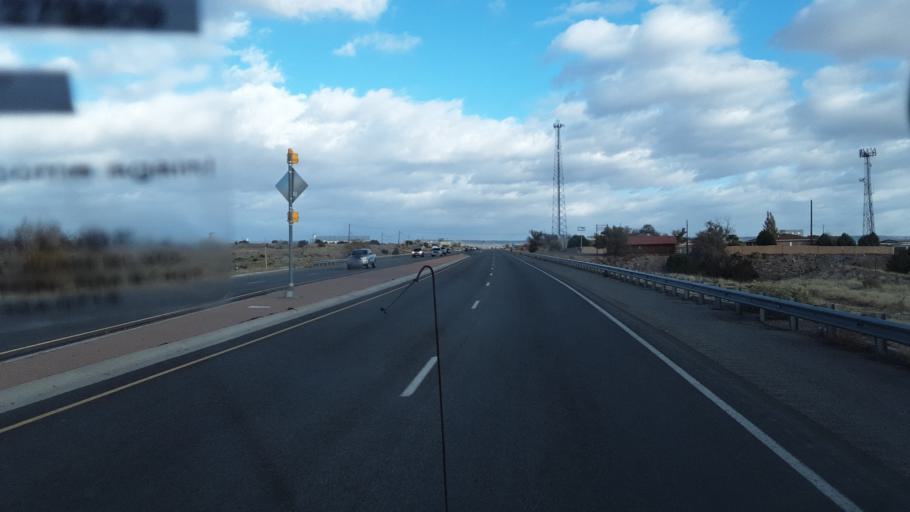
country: US
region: New Mexico
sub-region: Rio Arriba County
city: Espanola
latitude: 36.0104
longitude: -106.0883
